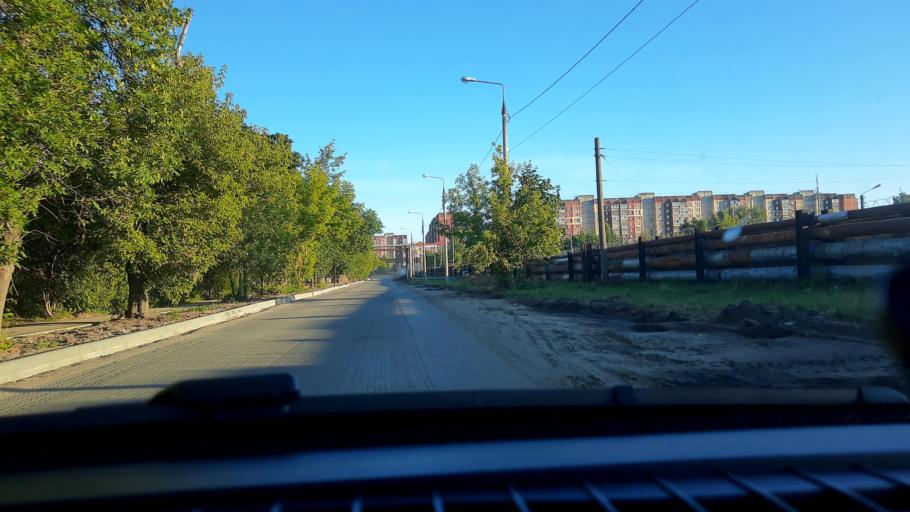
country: RU
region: Nizjnij Novgorod
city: Gorbatovka
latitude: 56.2428
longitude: 43.8277
